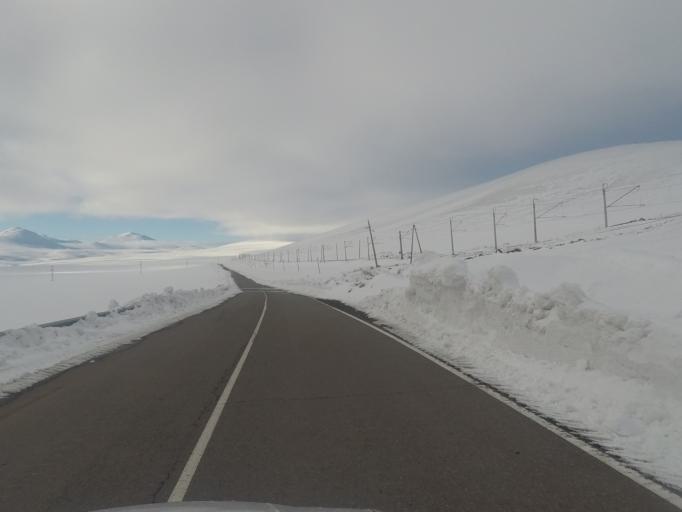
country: GE
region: Kvemo Kartli
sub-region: Tsalka
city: Tsalka
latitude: 41.4634
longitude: 43.8610
